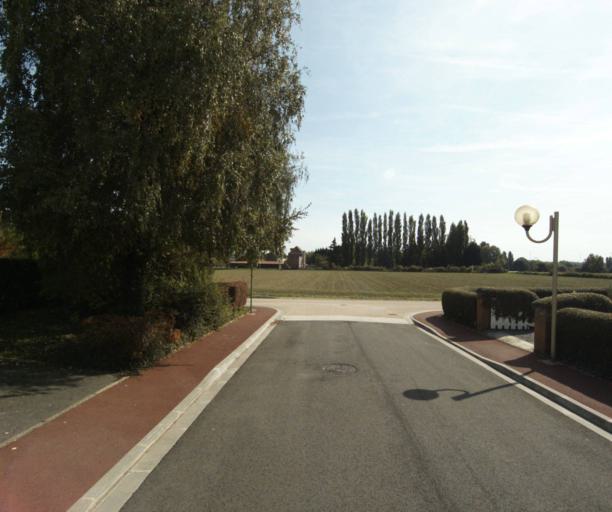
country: FR
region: Nord-Pas-de-Calais
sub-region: Departement du Nord
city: Hallennes-lez-Haubourdin
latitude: 50.6232
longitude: 2.9590
